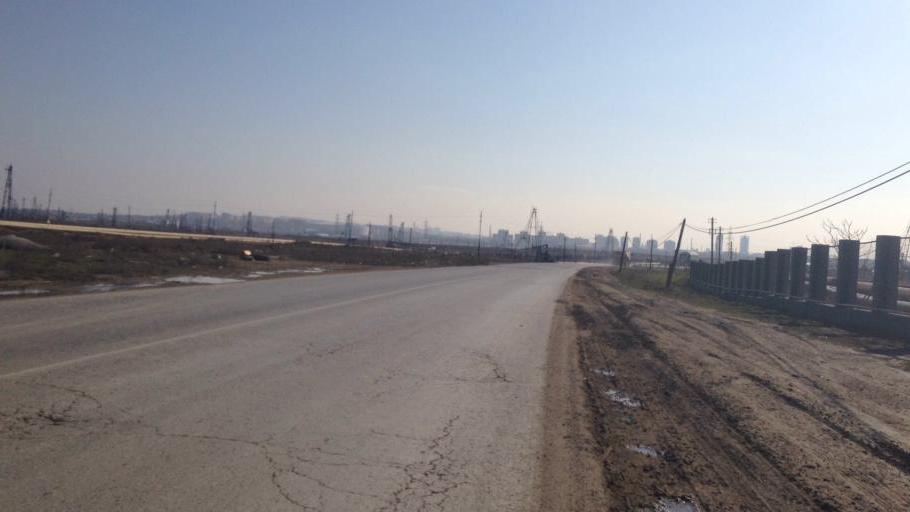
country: AZ
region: Baki
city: Balakhani
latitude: 40.4596
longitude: 49.8908
